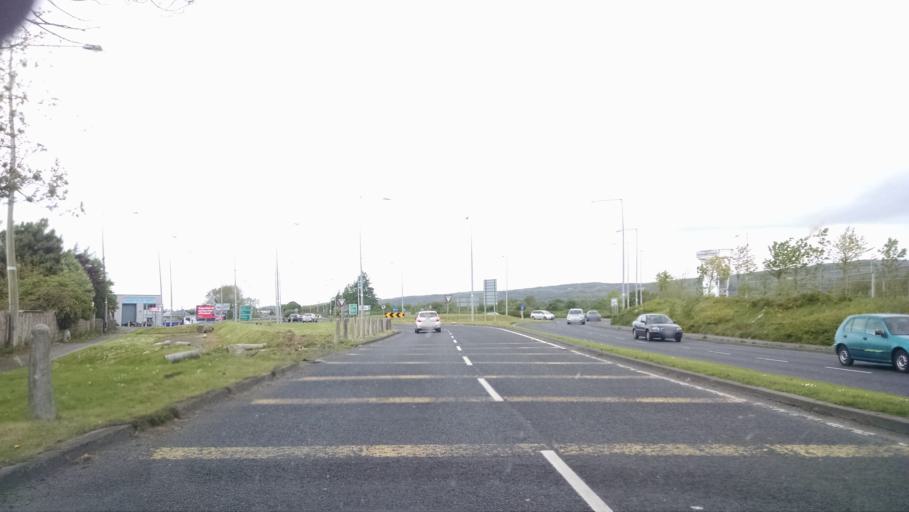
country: IE
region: Munster
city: Moyross
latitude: 52.6759
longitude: -8.6807
